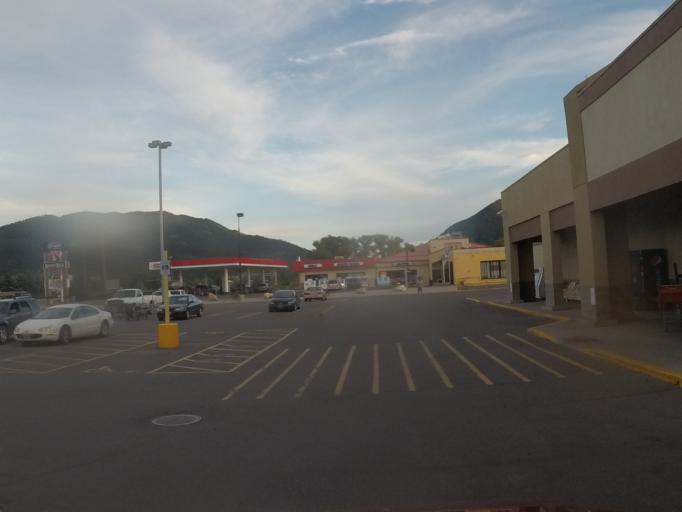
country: US
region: Montana
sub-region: Park County
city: Livingston
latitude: 45.6423
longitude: -110.5753
